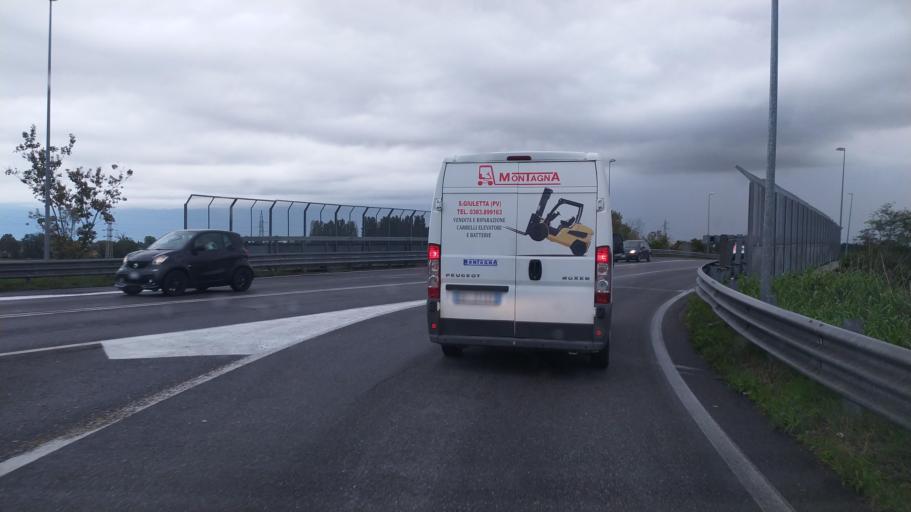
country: IT
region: Lombardy
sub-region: Provincia di Pavia
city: Pavia
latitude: 45.2091
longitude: 9.1499
